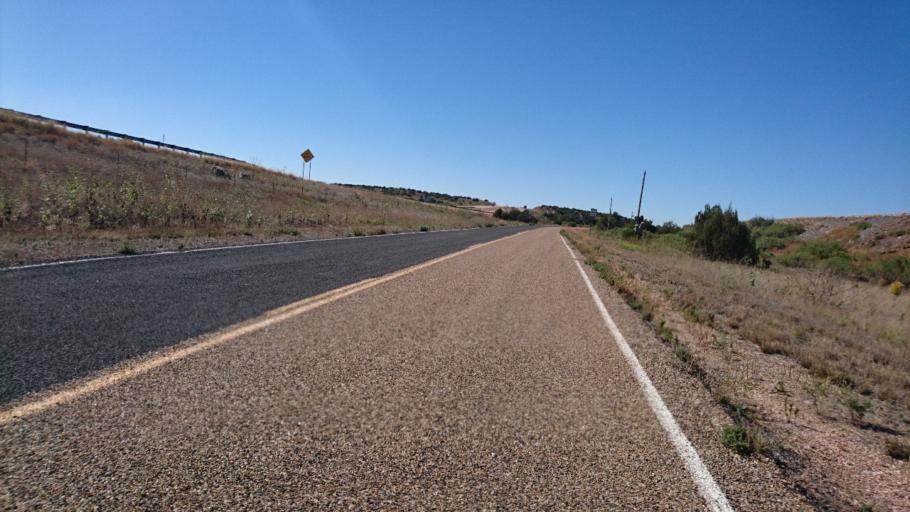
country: US
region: New Mexico
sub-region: Guadalupe County
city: Santa Rosa
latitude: 35.0694
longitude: -104.2084
